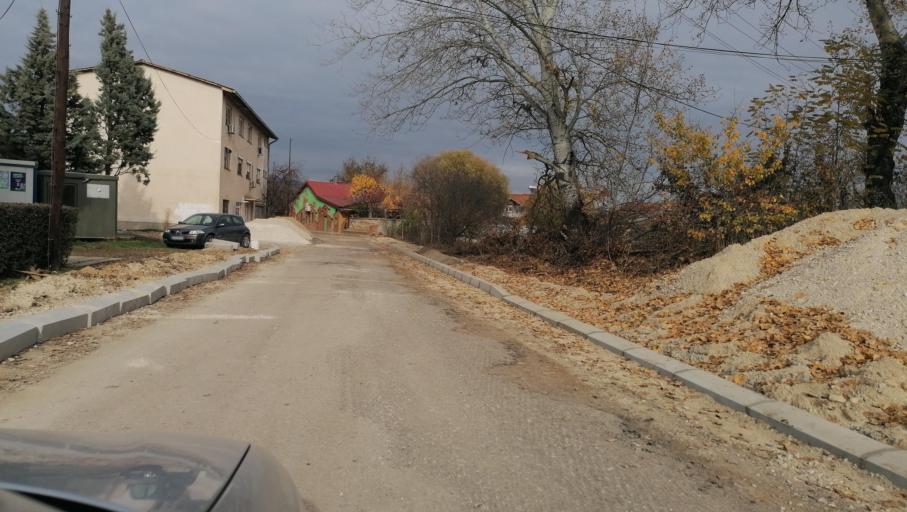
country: MK
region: Cesinovo-Oblesevo
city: Cesinovo
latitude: 41.8750
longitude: 22.2946
